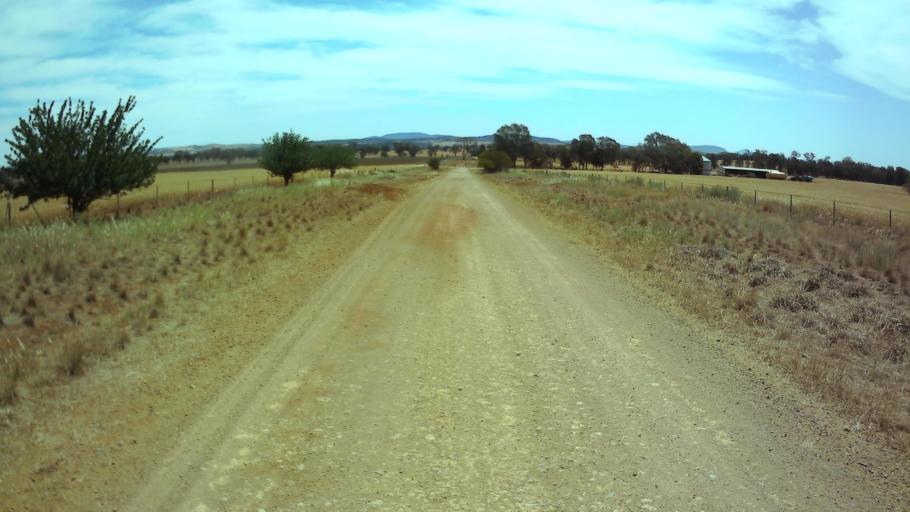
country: AU
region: New South Wales
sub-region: Weddin
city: Grenfell
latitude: -33.7492
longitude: 148.1495
